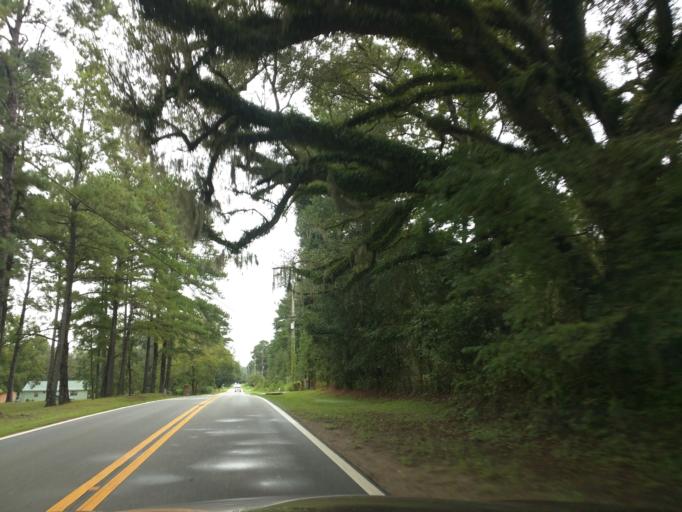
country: US
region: Florida
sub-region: Leon County
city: Tallahassee
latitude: 30.4933
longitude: -84.1255
